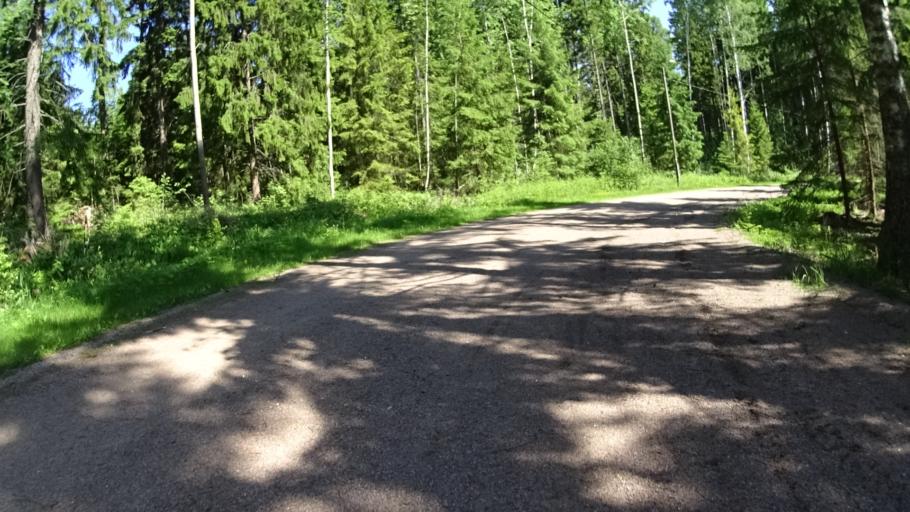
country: FI
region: Uusimaa
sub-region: Helsinki
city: Kilo
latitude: 60.2967
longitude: 24.8060
